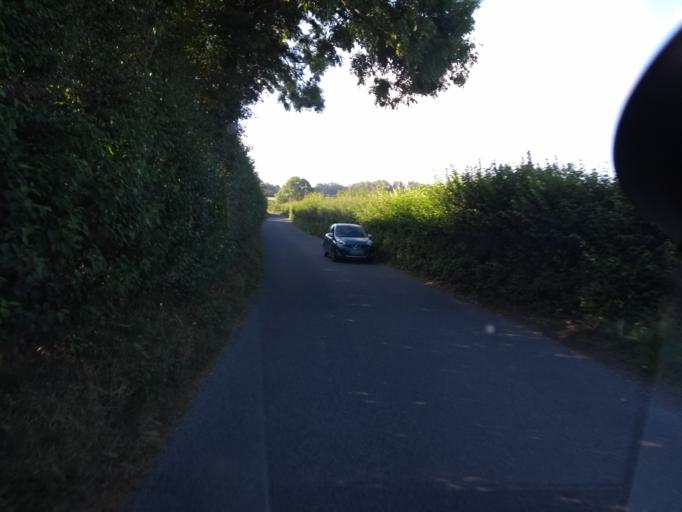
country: GB
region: England
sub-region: Somerset
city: South Petherton
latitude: 50.9639
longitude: -2.8087
